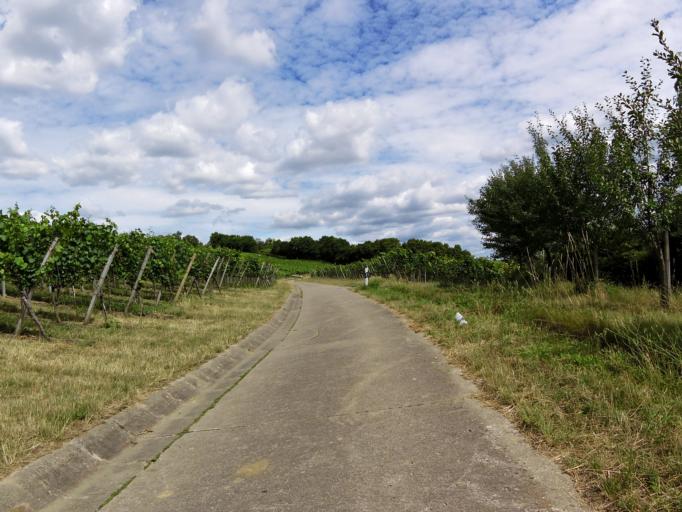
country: DE
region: Bavaria
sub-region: Regierungsbezirk Unterfranken
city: Veitshochheim
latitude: 49.8162
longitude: 9.8917
